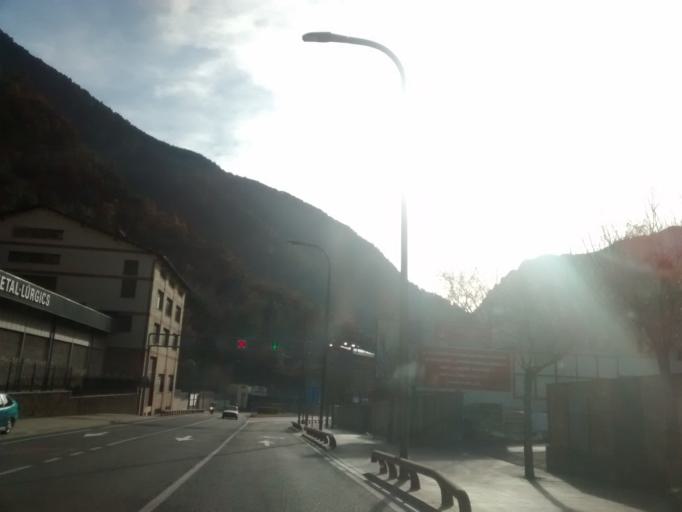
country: AD
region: Sant Julia de Loria
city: Sant Julia de Loria
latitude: 42.4908
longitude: 1.4963
